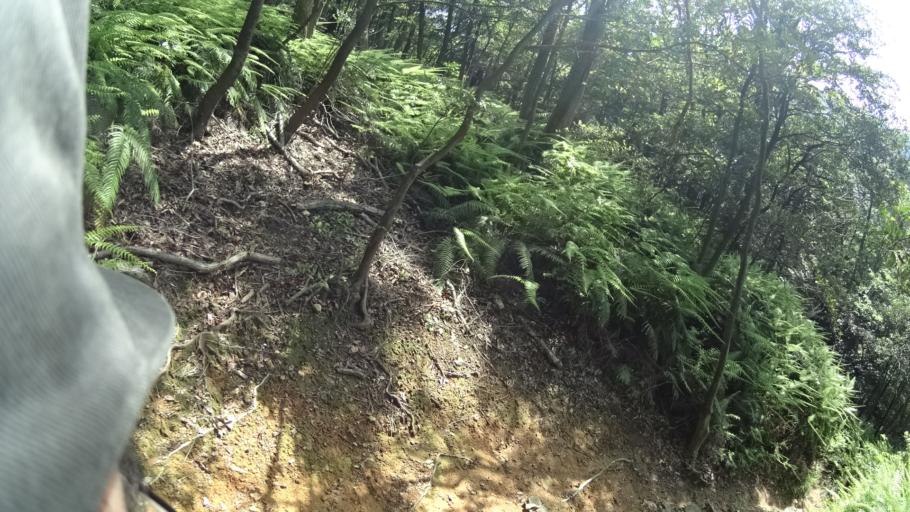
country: JP
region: Shizuoka
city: Kosai-shi
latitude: 34.7783
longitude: 137.4947
